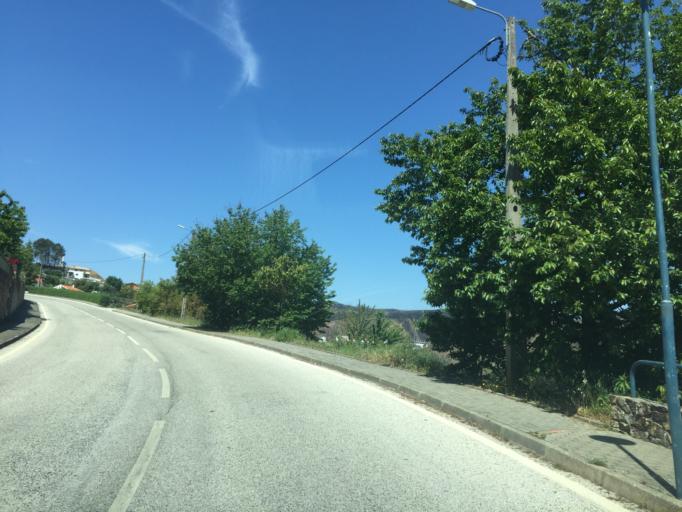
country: PT
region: Coimbra
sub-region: Pampilhosa da Serra
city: Pampilhosa da Serra
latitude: 40.0451
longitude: -7.9487
